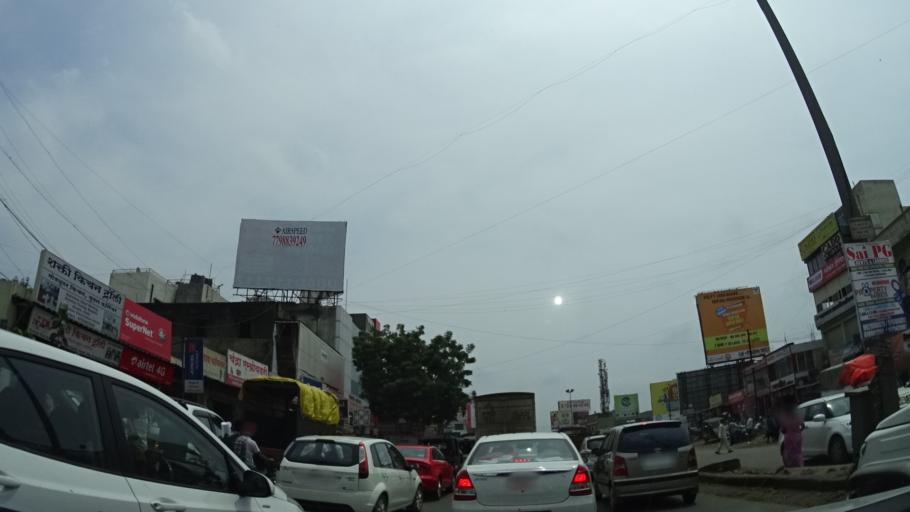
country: IN
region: Maharashtra
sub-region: Pune Division
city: Lohogaon
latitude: 18.5808
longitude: 73.9816
